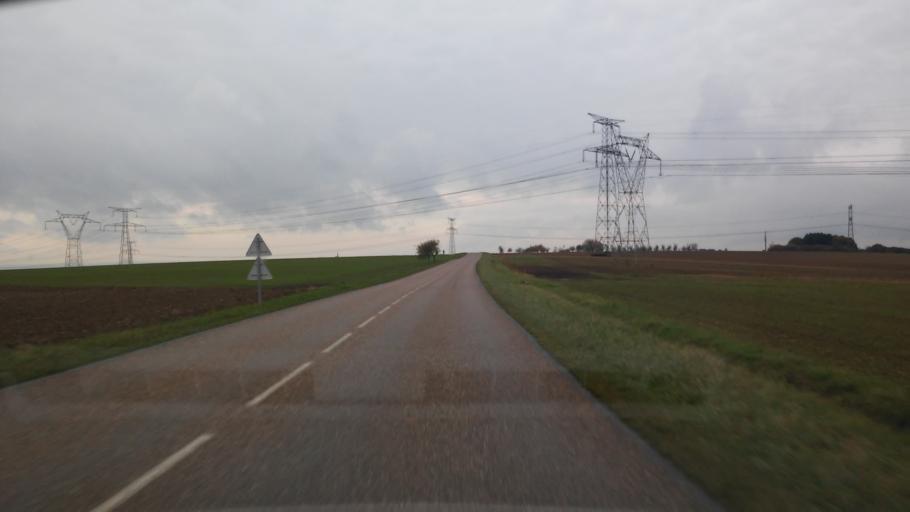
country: FR
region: Lorraine
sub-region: Departement de la Moselle
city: Vigy
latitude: 49.1866
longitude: 6.3072
